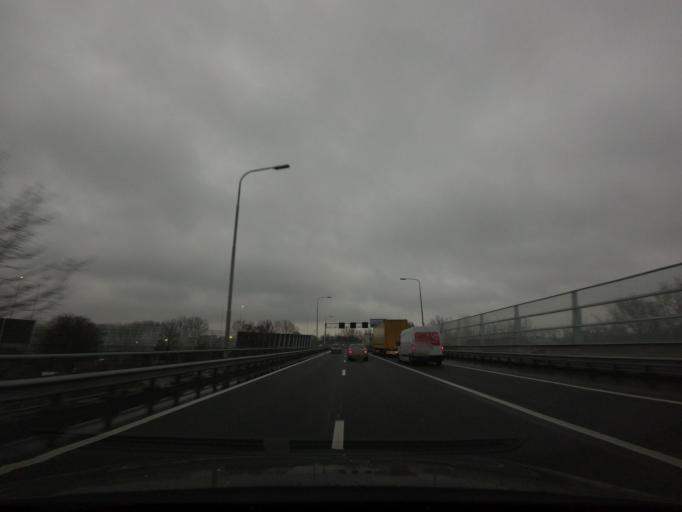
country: NL
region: South Holland
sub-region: Gemeente Vlaardingen
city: Vlaardingen
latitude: 51.9235
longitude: 4.3641
